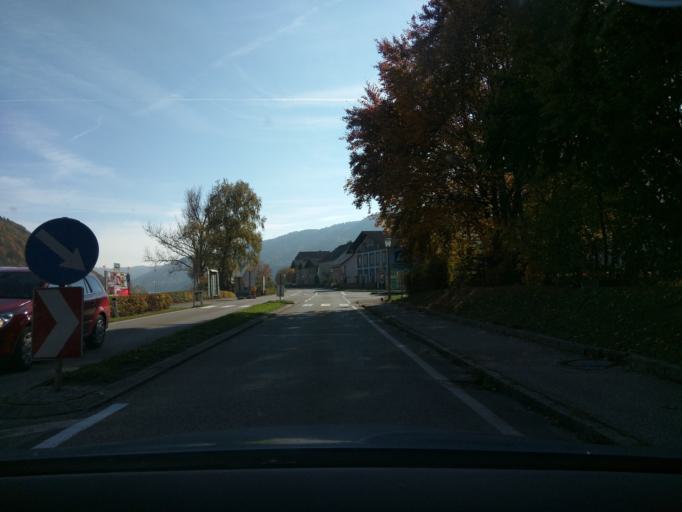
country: AT
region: Upper Austria
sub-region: Politischer Bezirk Rohrbach
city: Pfarrkirchen im Muehlkreis
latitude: 48.5053
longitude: 13.7340
